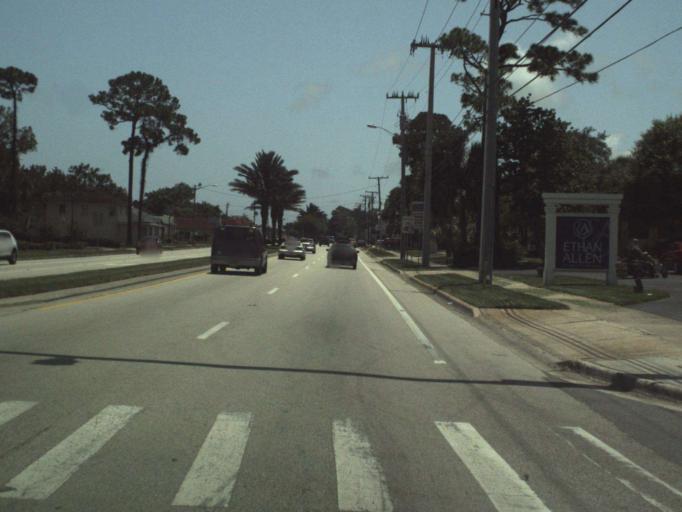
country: US
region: Florida
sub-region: Volusia County
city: Ormond Beach
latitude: 29.2718
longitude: -81.0564
